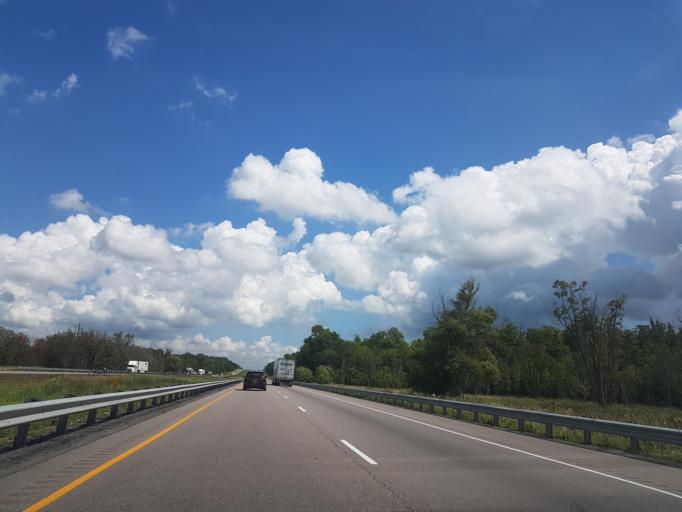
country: CA
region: Ontario
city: Skatepark
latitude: 44.2773
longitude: -76.8325
